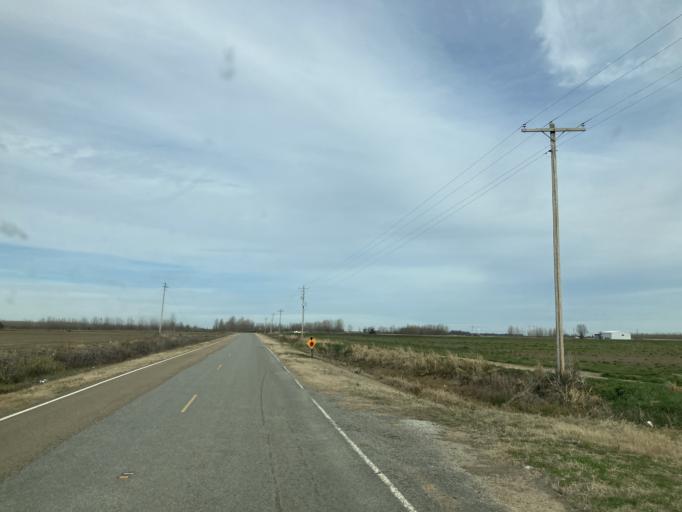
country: US
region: Mississippi
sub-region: Humphreys County
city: Belzoni
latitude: 33.1799
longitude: -90.6065
